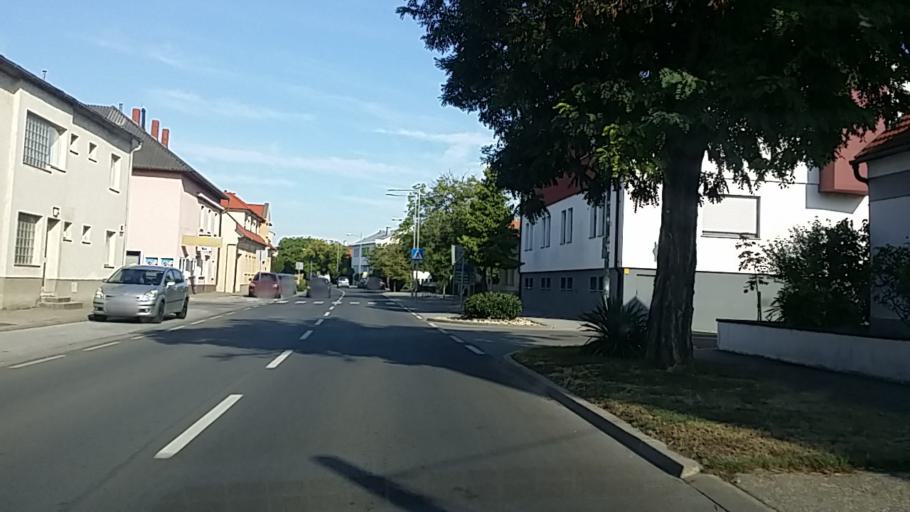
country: AT
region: Burgenland
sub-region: Politischer Bezirk Neusiedl am See
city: Illmitz
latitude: 47.7604
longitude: 16.8079
